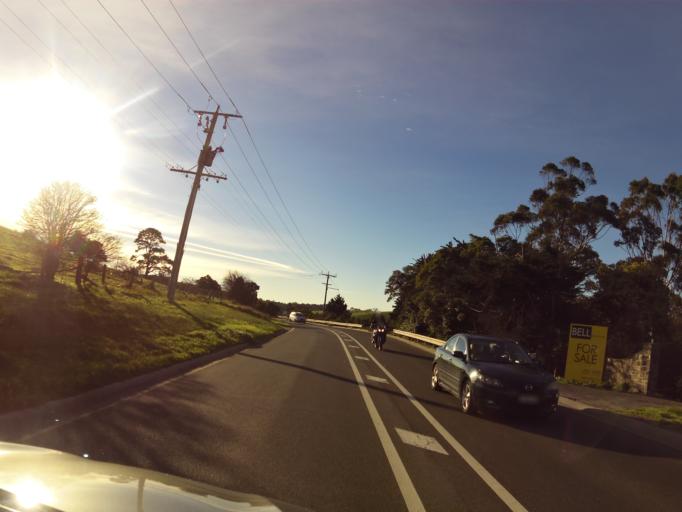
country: AU
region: Victoria
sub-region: Yarra Ranges
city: Lysterfield
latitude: -37.9156
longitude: 145.2996
